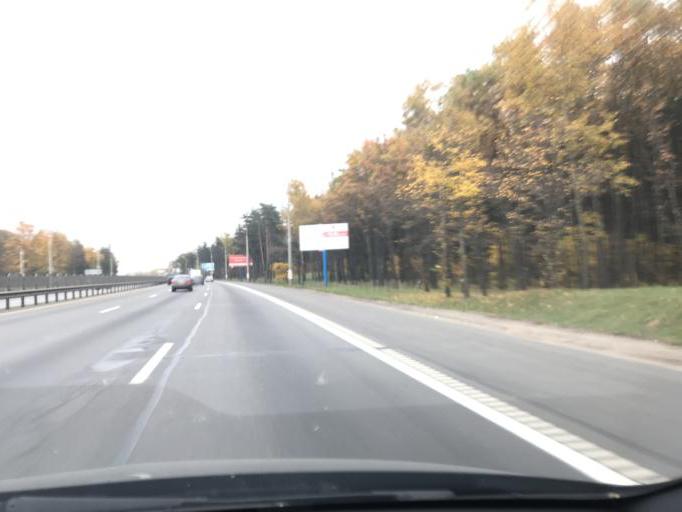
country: BY
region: Minsk
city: Hatava
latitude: 53.8335
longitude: 27.6415
